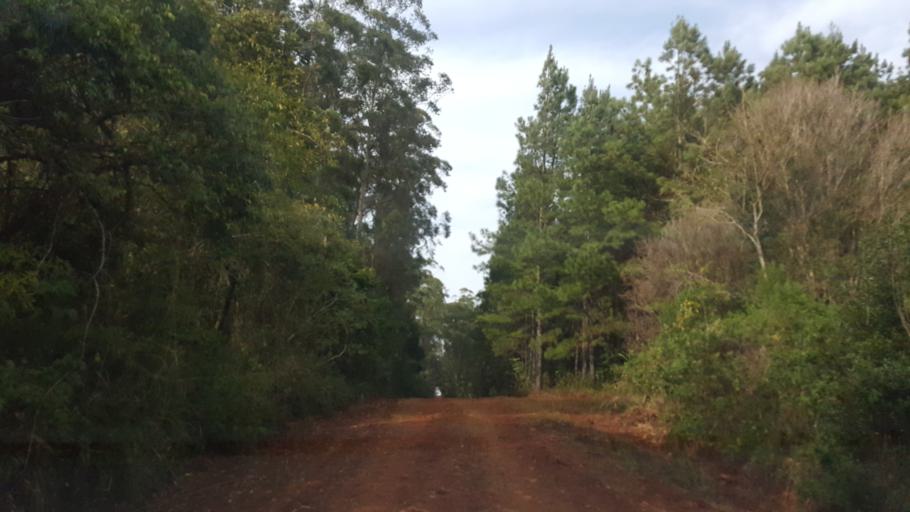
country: AR
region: Misiones
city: Capiovi
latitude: -26.9076
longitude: -55.1170
